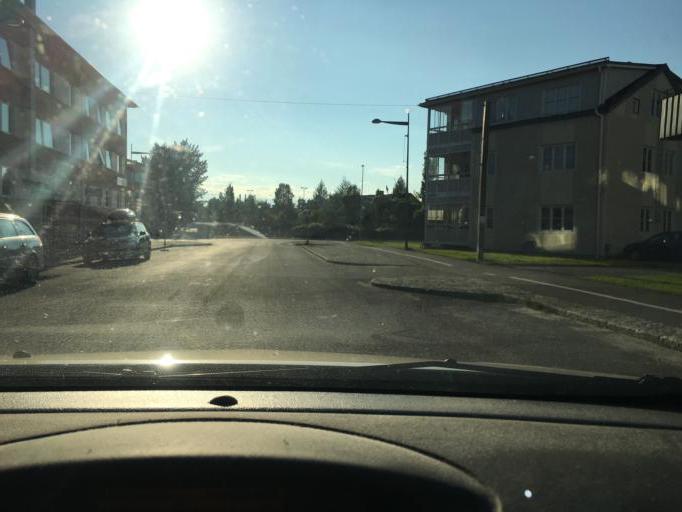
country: SE
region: Norrbotten
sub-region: Bodens Kommun
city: Boden
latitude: 65.8250
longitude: 21.6827
